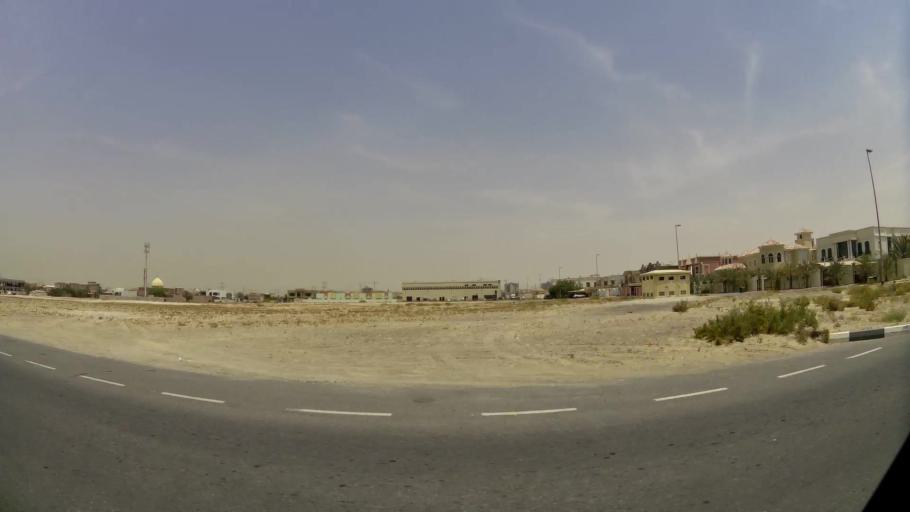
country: AE
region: Ash Shariqah
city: Sharjah
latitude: 25.1955
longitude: 55.3805
